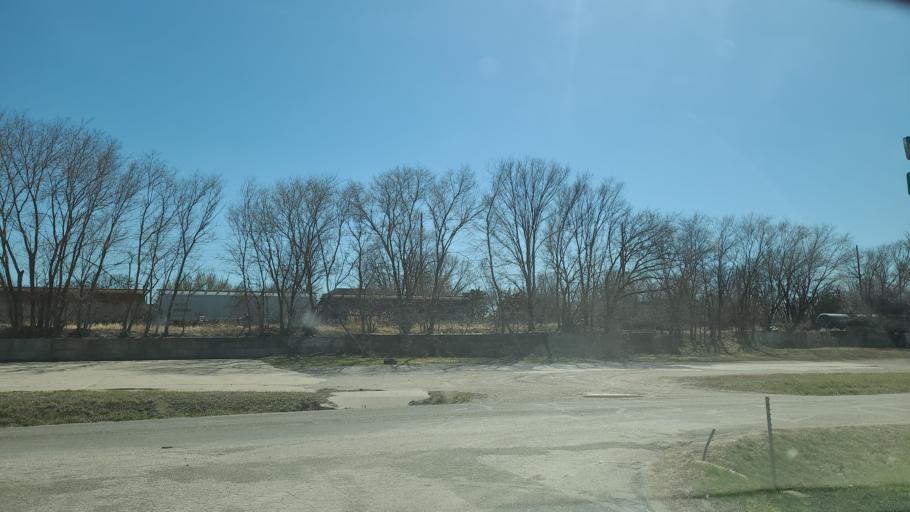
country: US
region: Kansas
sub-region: Douglas County
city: Lawrence
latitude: 38.9789
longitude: -95.2285
